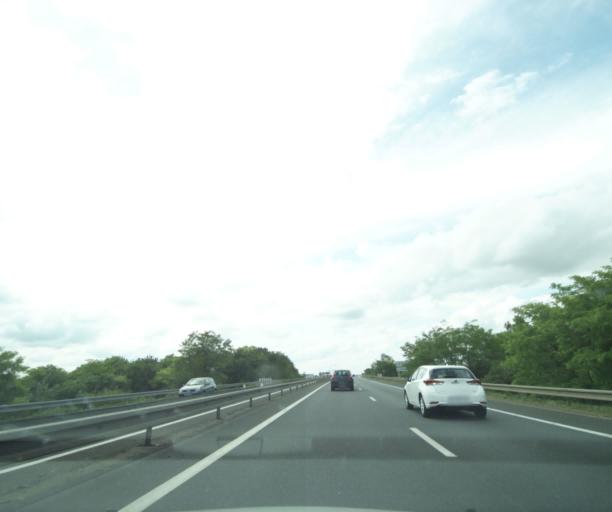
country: FR
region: Centre
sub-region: Departement du Cher
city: La Chapelle-Saint-Ursin
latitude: 47.0457
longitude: 2.3314
